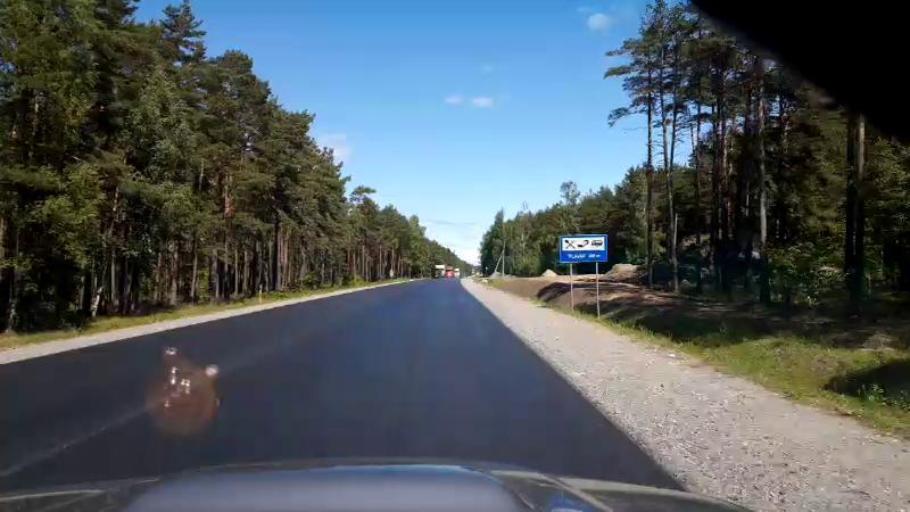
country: LV
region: Salacgrivas
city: Ainazi
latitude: 57.8394
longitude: 24.3476
